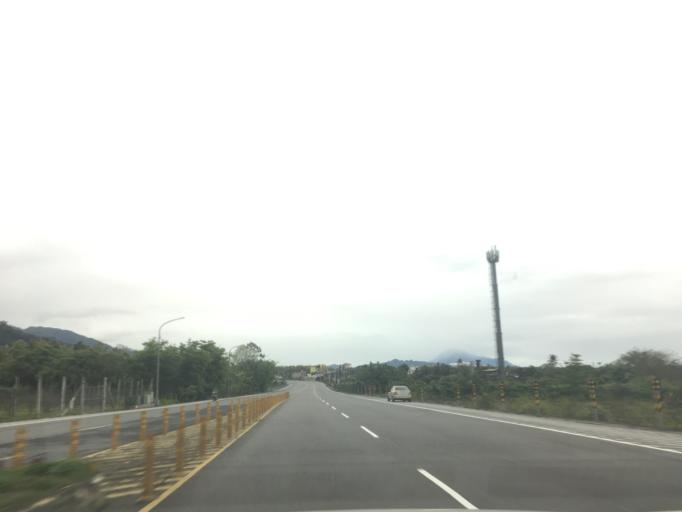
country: TW
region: Taiwan
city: Taitung City
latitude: 22.7235
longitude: 121.0549
